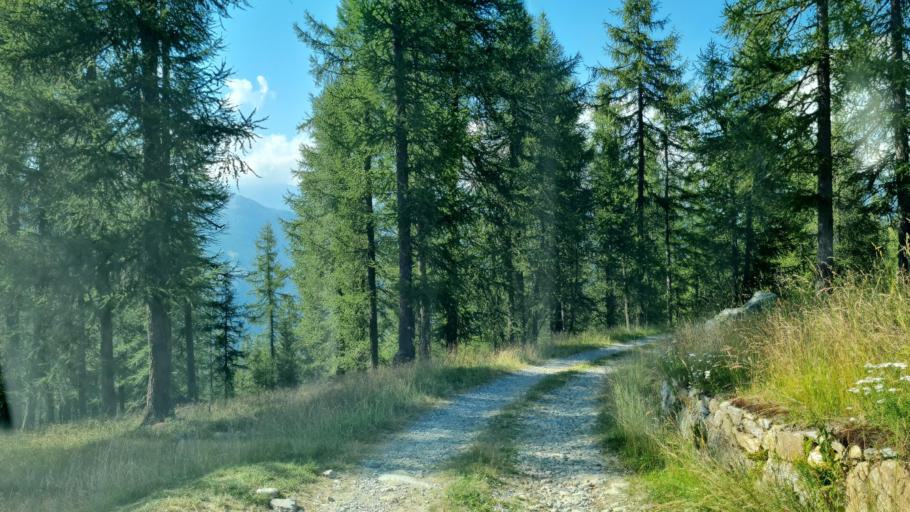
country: IT
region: Aosta Valley
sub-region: Valle d'Aosta
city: Fontainemore
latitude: 45.6234
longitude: 7.8740
